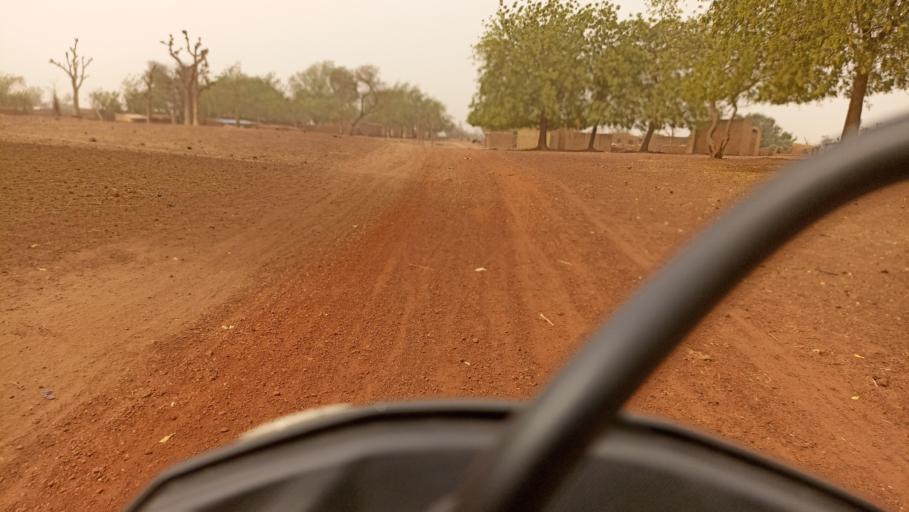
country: BF
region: Nord
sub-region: Province du Zondoma
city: Gourcy
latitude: 13.2659
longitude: -2.5426
